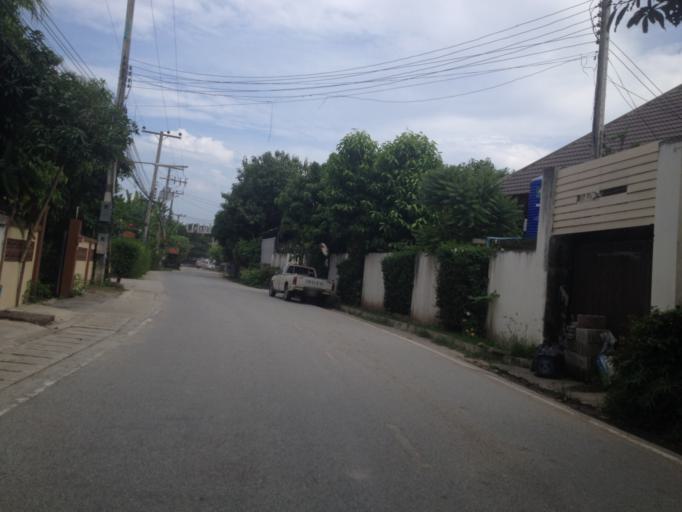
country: TH
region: Chiang Mai
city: Hang Dong
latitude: 18.6817
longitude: 98.9524
